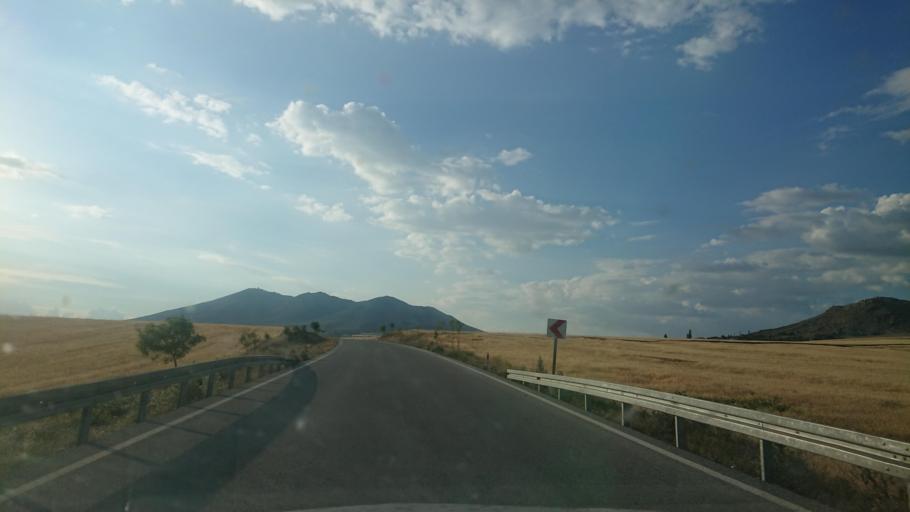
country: TR
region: Aksaray
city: Balci
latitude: 38.5814
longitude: 34.1045
